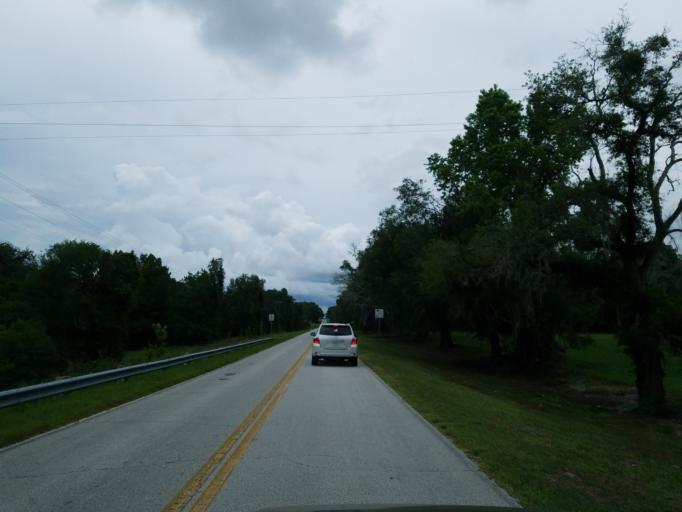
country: US
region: Florida
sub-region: Alachua County
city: High Springs
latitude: 29.9442
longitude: -82.5069
